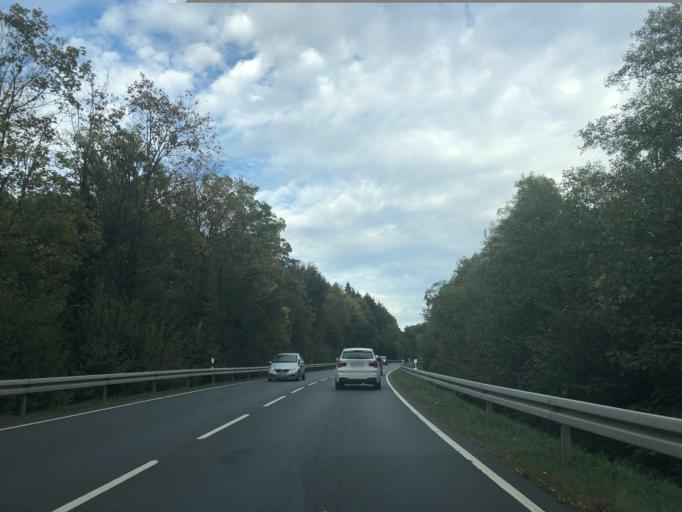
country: DE
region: Hesse
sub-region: Regierungsbezirk Darmstadt
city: Konigstein im Taunus
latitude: 50.1699
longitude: 8.4660
